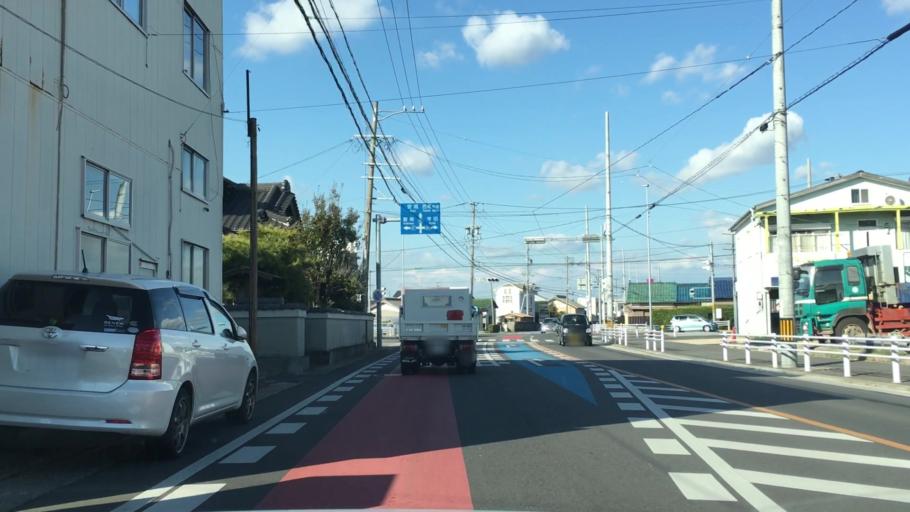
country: JP
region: Aichi
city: Nishio
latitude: 34.8389
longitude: 137.0463
